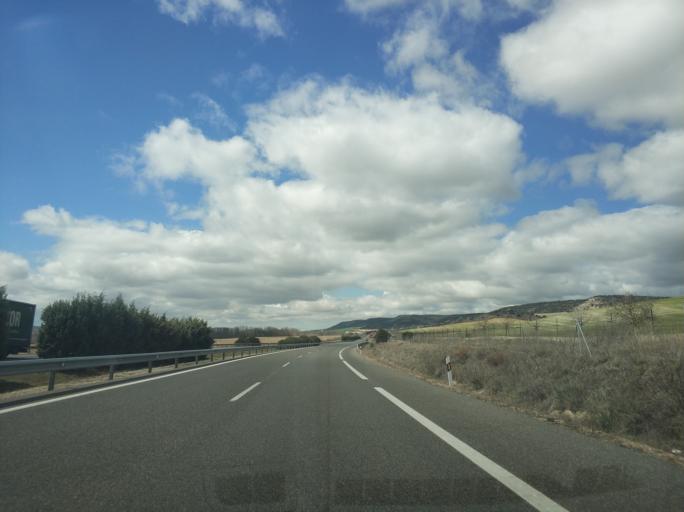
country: ES
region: Castille and Leon
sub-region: Provincia de Palencia
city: Quintana del Puente
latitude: 42.1083
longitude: -4.1764
